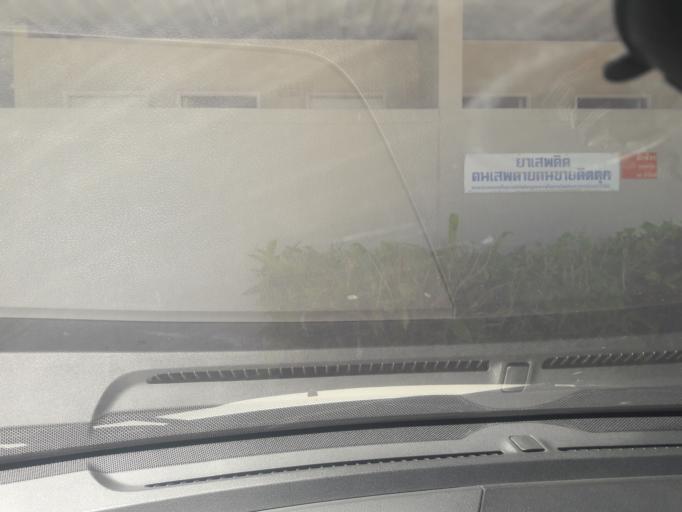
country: TH
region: Chiang Mai
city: San Kamphaeng
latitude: 18.7469
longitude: 99.1148
